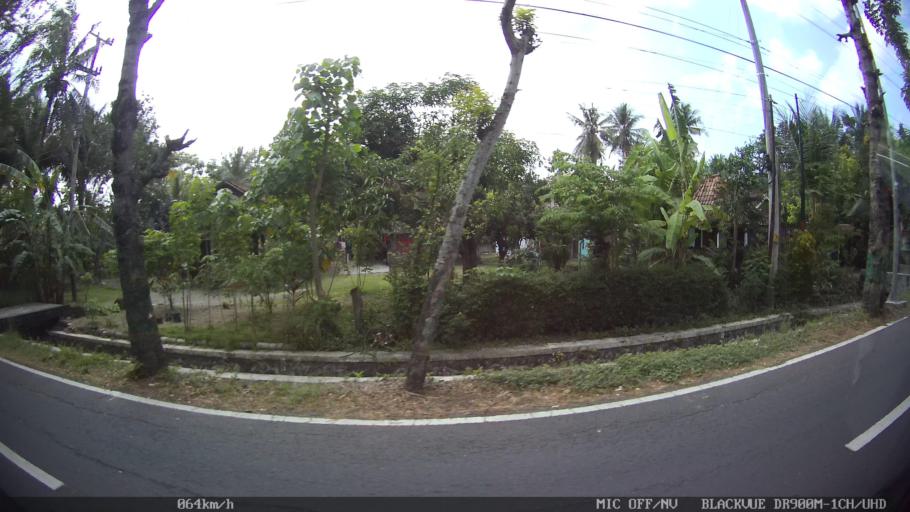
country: ID
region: Daerah Istimewa Yogyakarta
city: Srandakan
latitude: -7.8788
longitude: 110.1327
